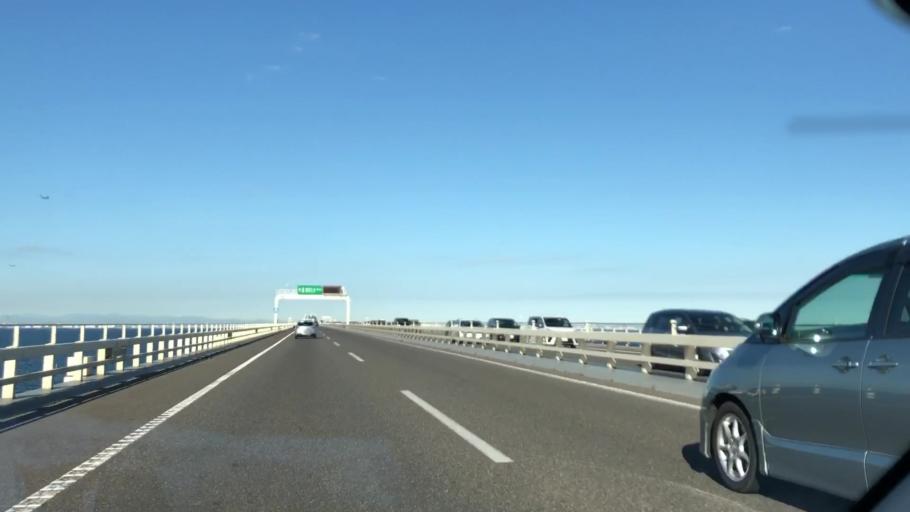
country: JP
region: Chiba
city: Kisarazu
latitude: 35.4427
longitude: 139.9061
